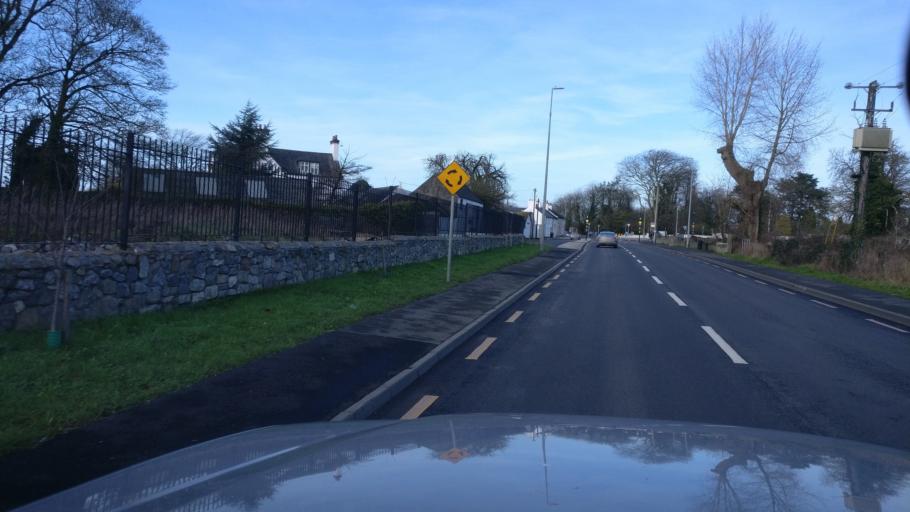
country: IE
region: Leinster
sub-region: Laois
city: Mountmellick
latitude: 53.1102
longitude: -7.3286
